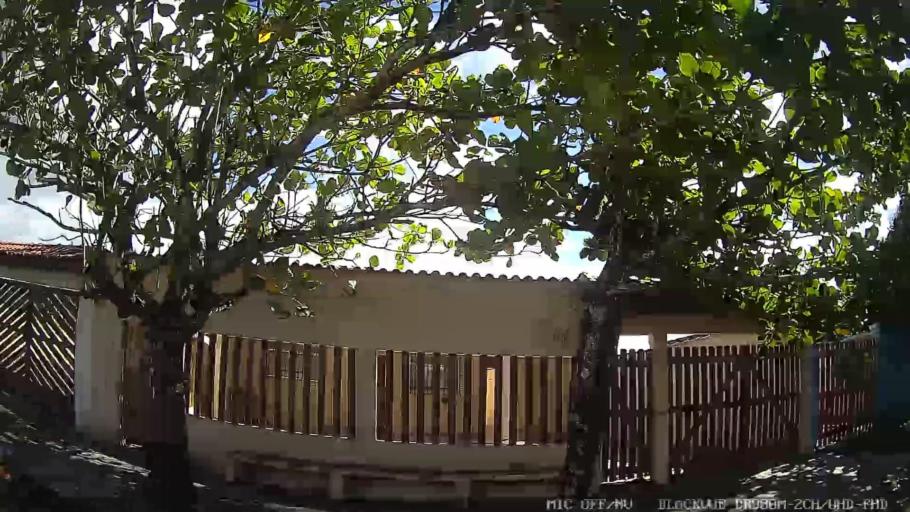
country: BR
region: Sao Paulo
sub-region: Itanhaem
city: Itanhaem
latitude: -24.2388
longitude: -46.8843
